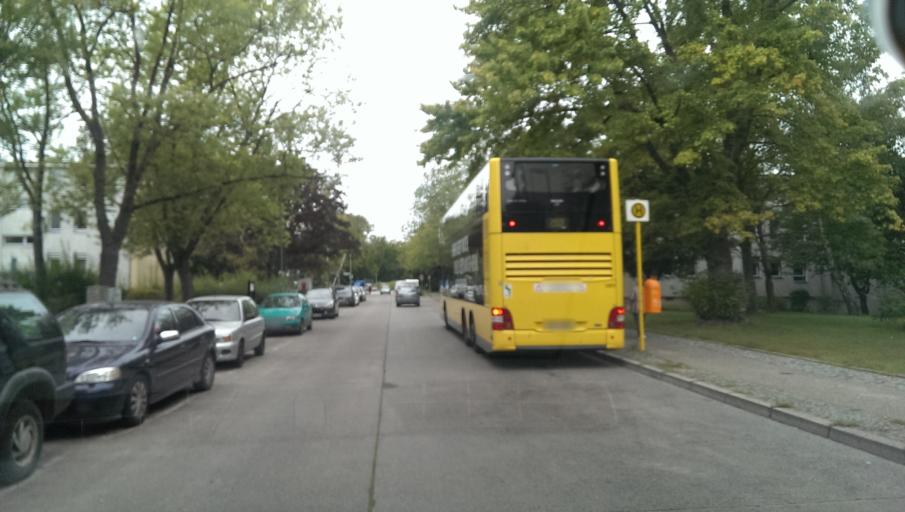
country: DE
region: Berlin
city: Britz
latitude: 52.4449
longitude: 13.4101
